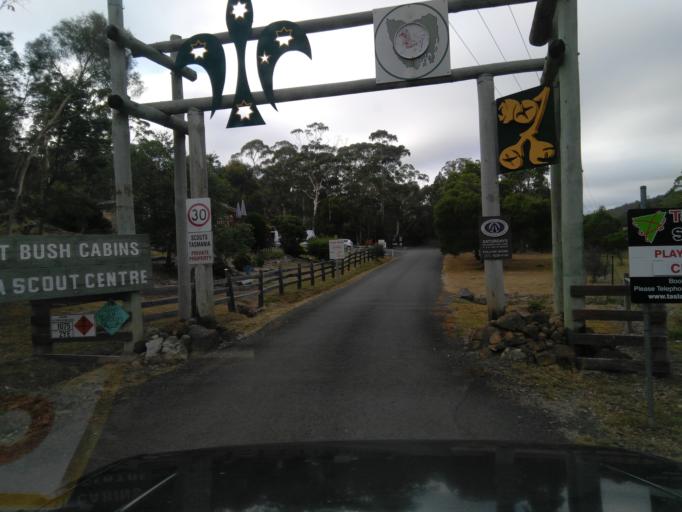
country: AU
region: Tasmania
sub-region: Kingborough
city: Kingston
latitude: -42.9423
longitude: 147.3128
